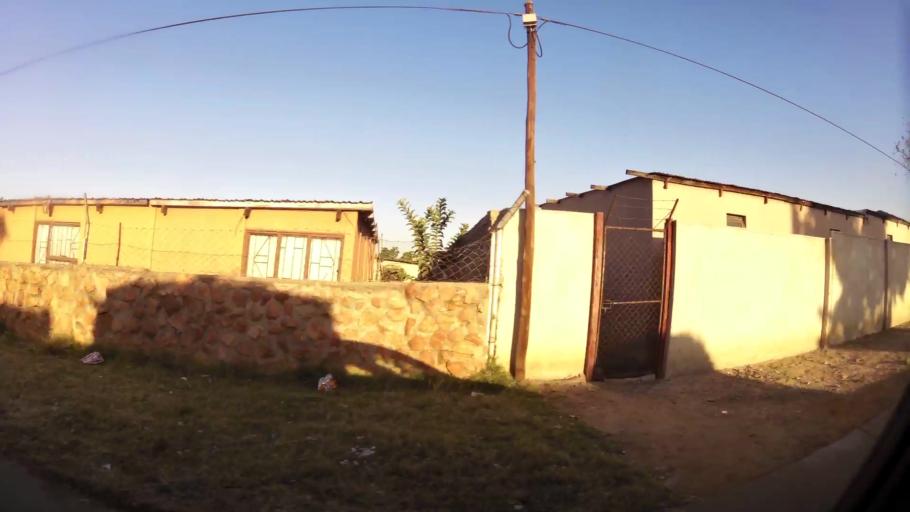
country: ZA
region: North-West
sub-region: Bojanala Platinum District Municipality
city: Rustenburg
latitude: -25.6440
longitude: 27.2107
